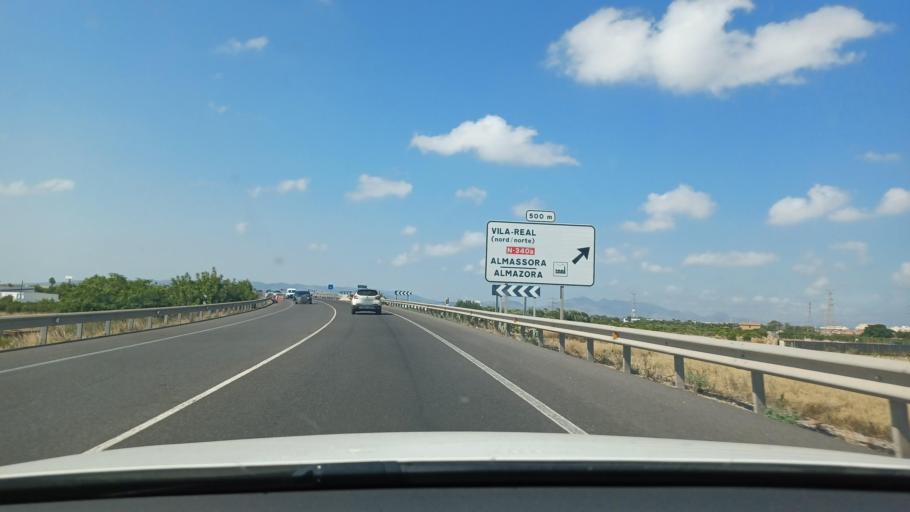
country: ES
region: Valencia
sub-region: Provincia de Castello
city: Vila-real
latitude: 39.9398
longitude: -0.0862
